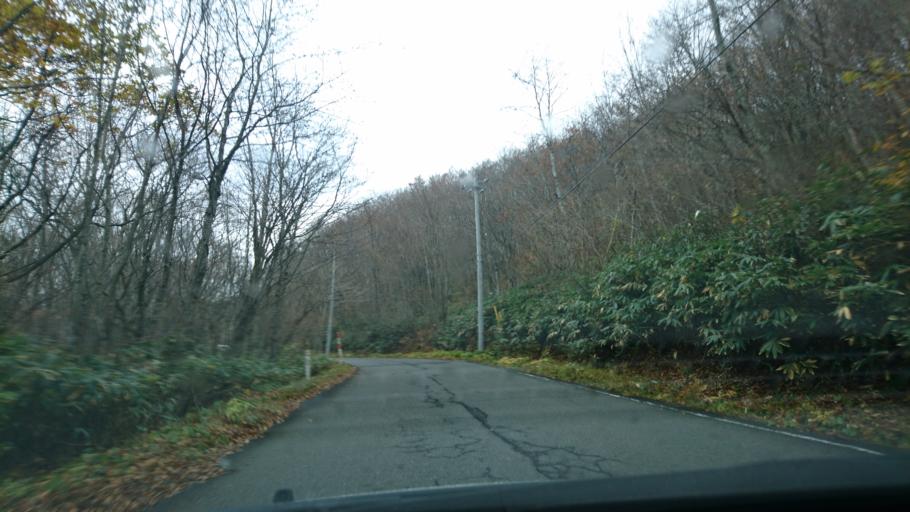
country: JP
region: Iwate
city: Ichinoseki
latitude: 38.9183
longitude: 140.8450
